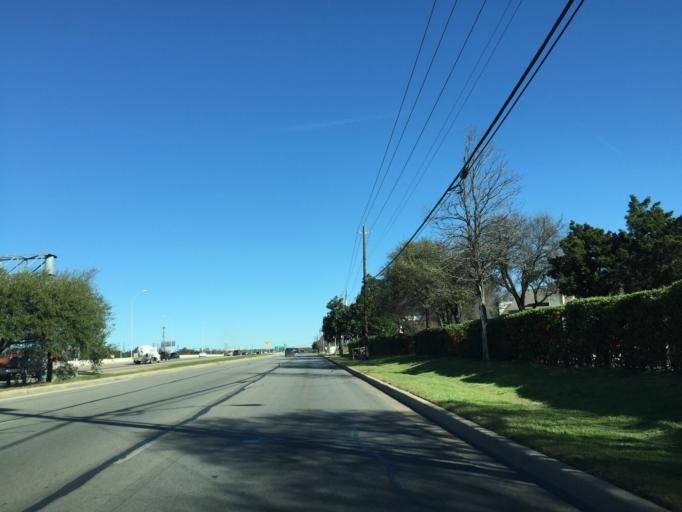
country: US
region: Texas
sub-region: Williamson County
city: Jollyville
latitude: 30.4117
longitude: -97.7450
